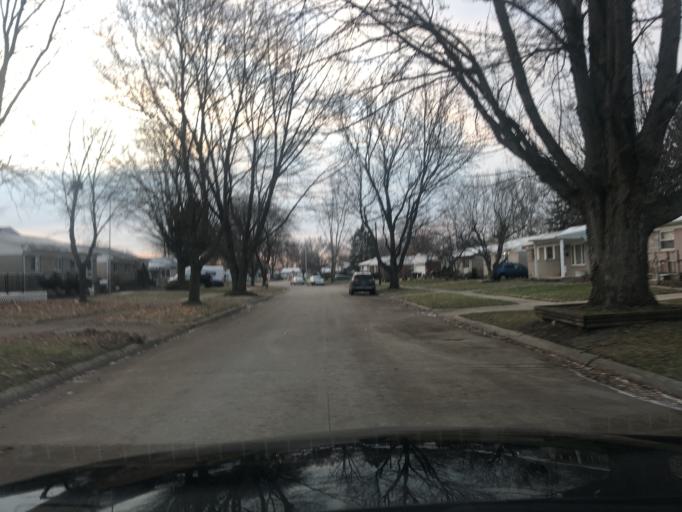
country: US
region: Michigan
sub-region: Wayne County
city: Romulus
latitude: 42.2347
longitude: -83.3822
